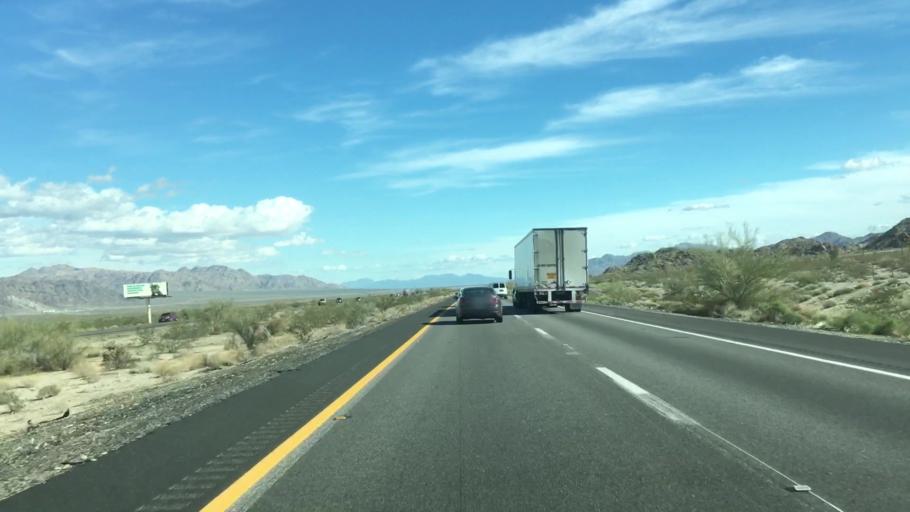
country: US
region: California
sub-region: Riverside County
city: Mecca
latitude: 33.6636
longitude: -115.6985
